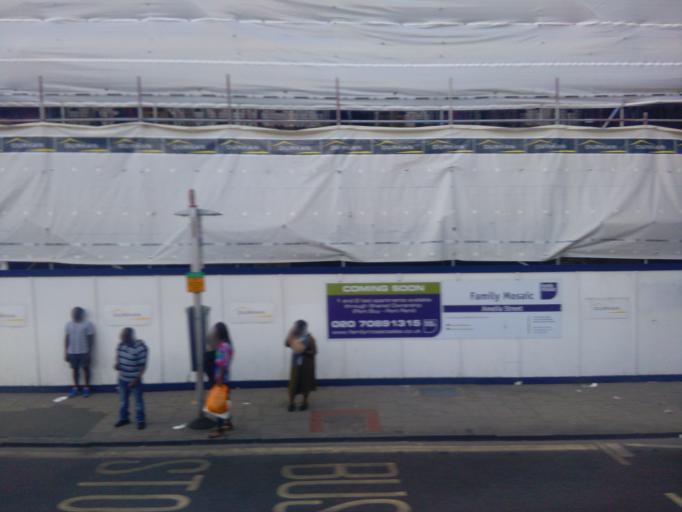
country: GB
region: England
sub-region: Greater London
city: Kennington
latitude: 51.4906
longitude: -0.0972
